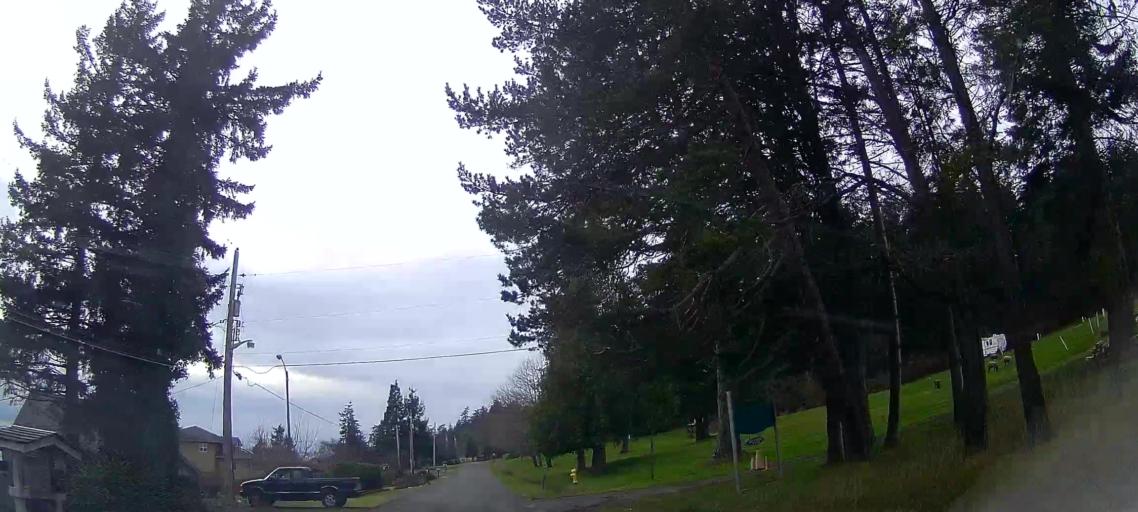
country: US
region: Washington
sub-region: Skagit County
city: Anacortes
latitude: 48.5686
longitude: -122.4945
